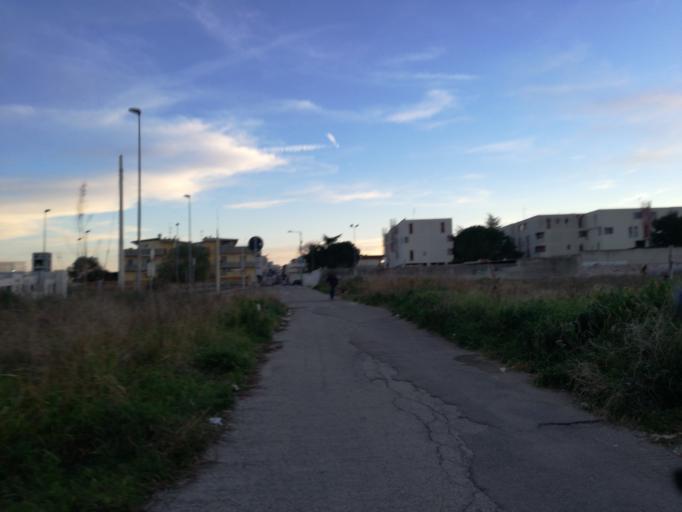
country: IT
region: Apulia
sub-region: Provincia di Bari
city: Adelfia
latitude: 41.0078
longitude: 16.8715
